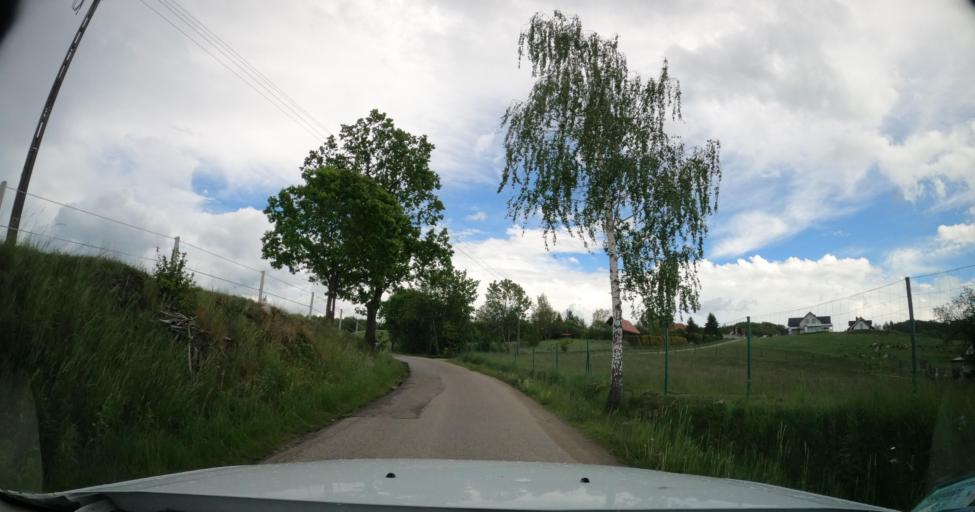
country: PL
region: Pomeranian Voivodeship
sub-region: Powiat kartuski
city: Garcz
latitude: 54.3366
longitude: 18.1408
